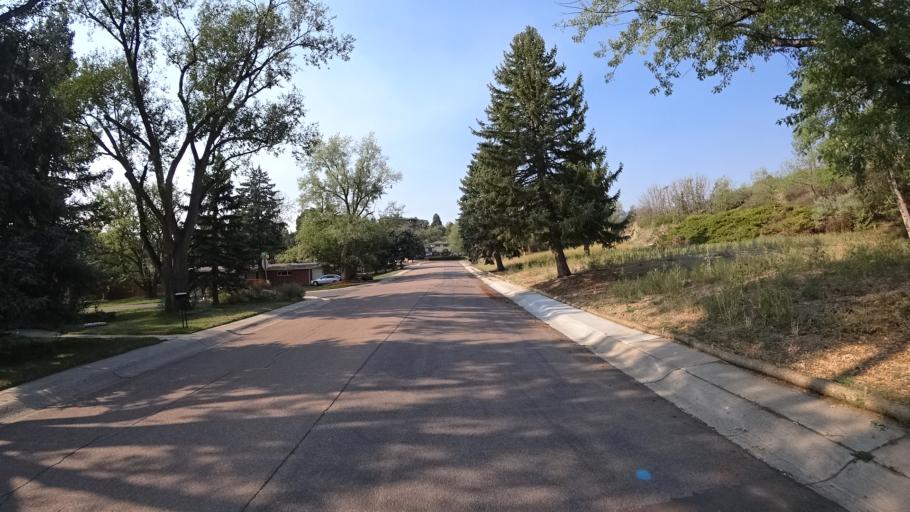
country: US
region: Colorado
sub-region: El Paso County
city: Colorado Springs
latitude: 38.8124
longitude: -104.8517
